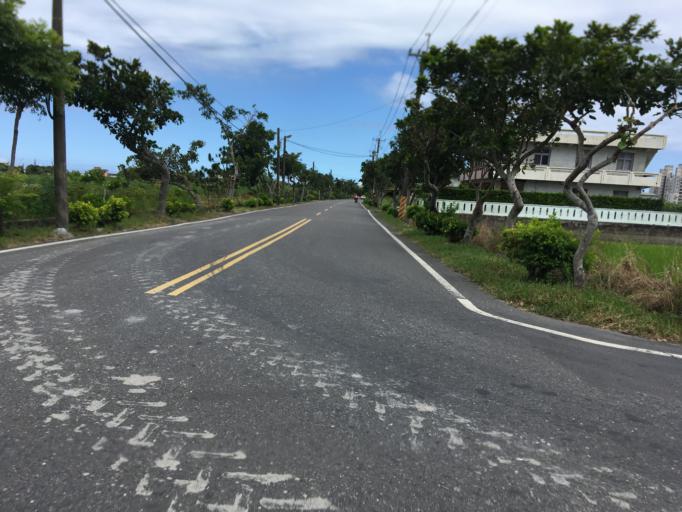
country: TW
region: Taiwan
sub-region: Yilan
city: Yilan
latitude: 24.6842
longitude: 121.8054
